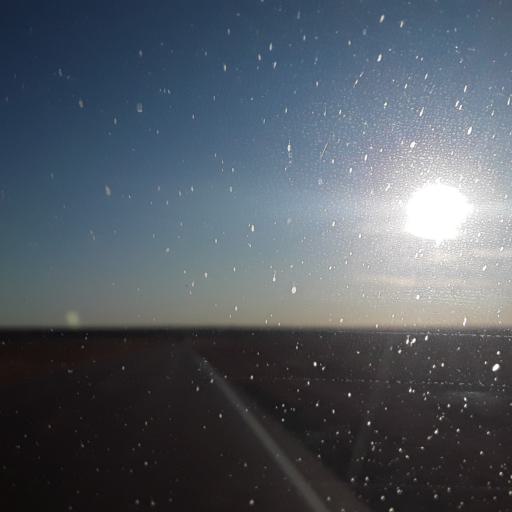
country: US
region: Kansas
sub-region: Wallace County
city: Sharon Springs
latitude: 38.9589
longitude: -101.7430
